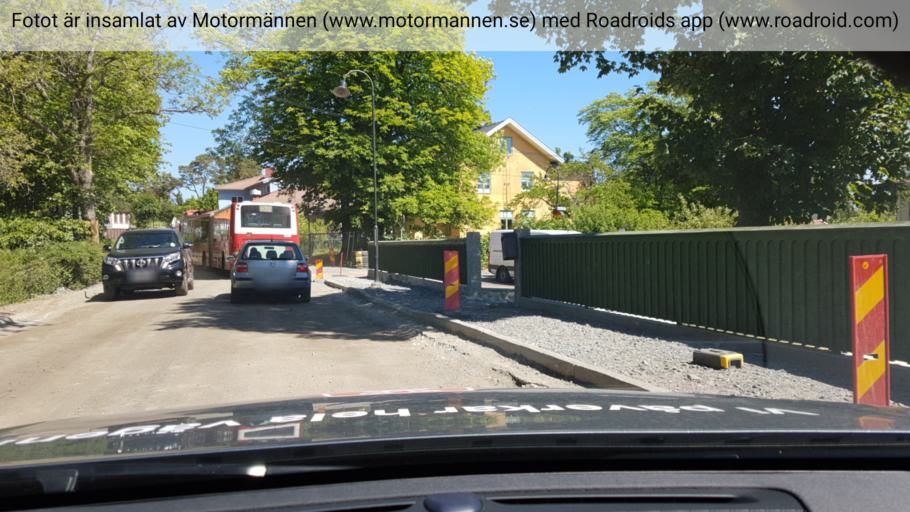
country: SE
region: Stockholm
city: Dalaro
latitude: 59.1339
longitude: 18.4089
